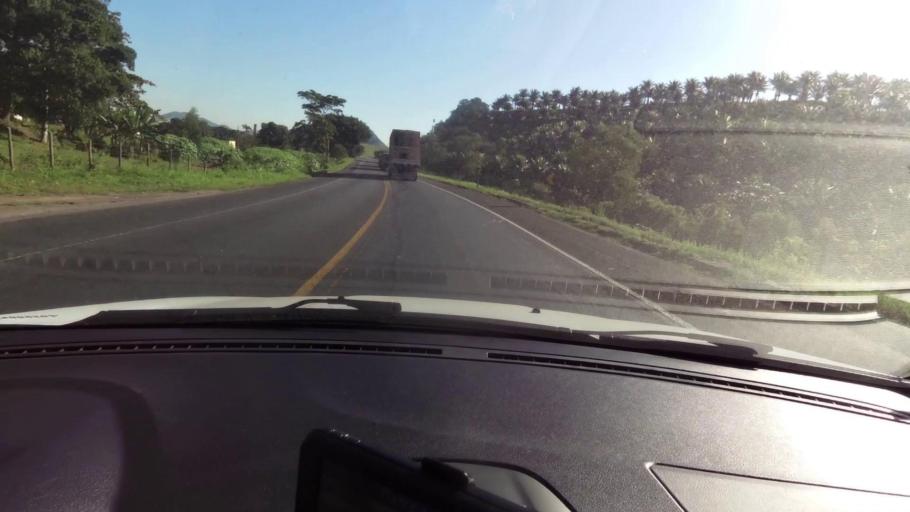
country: BR
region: Espirito Santo
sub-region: Alfredo Chaves
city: Alfredo Chaves
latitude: -20.6847
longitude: -40.6723
